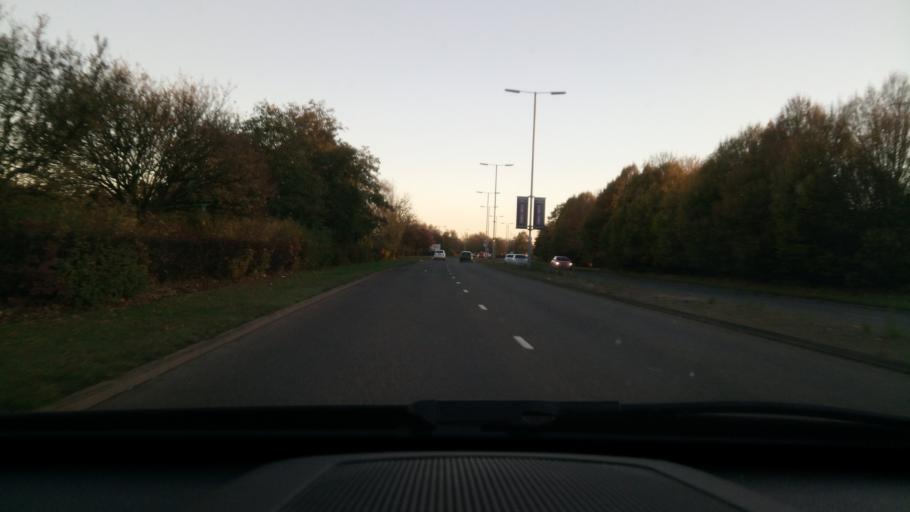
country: GB
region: England
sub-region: Peterborough
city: Peterborough
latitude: 52.5933
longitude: -0.2579
